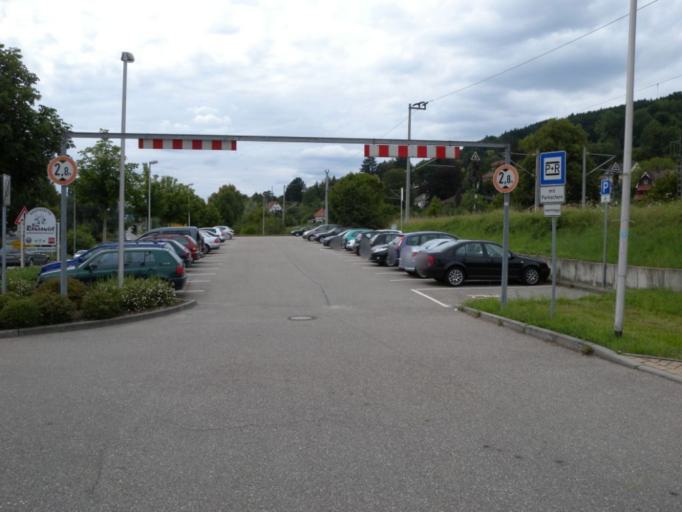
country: DE
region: Baden-Wuerttemberg
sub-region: Regierungsbezirk Stuttgart
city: Murrhardt
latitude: 48.9829
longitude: 9.5764
